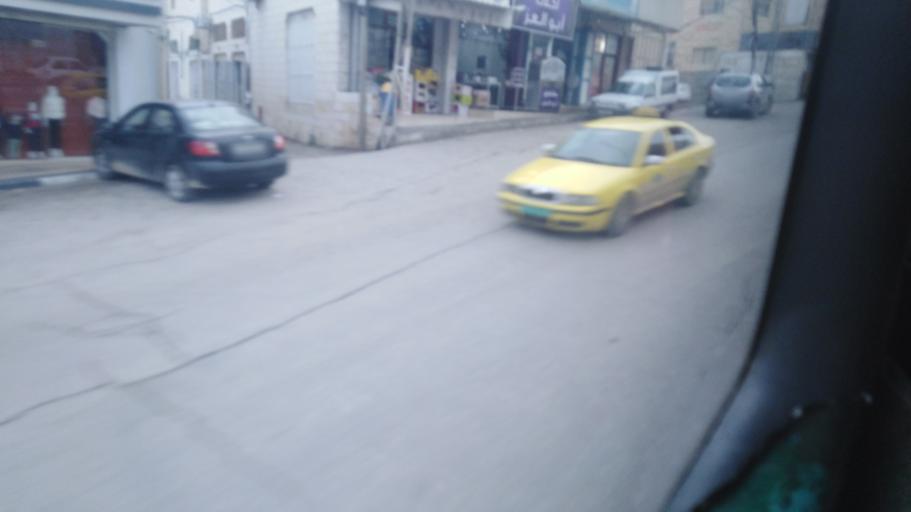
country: PS
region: West Bank
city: Hebron
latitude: 31.5273
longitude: 35.0864
